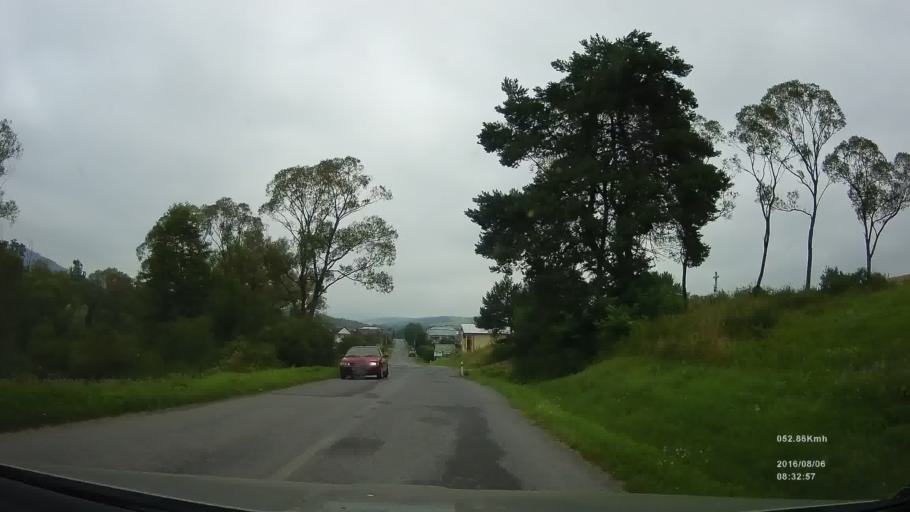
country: SK
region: Presovsky
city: Svidnik
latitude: 49.3401
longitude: 21.5973
